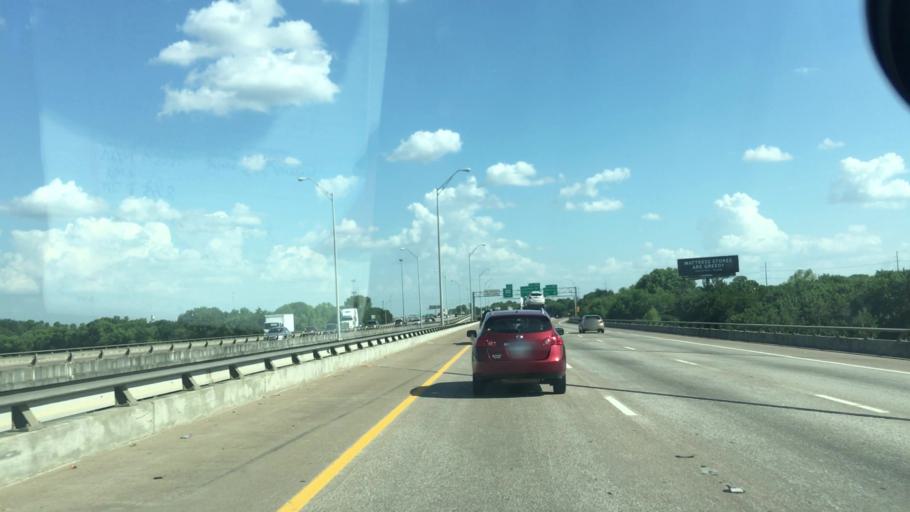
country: US
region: Texas
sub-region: Dallas County
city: Dallas
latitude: 32.7294
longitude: -96.7639
